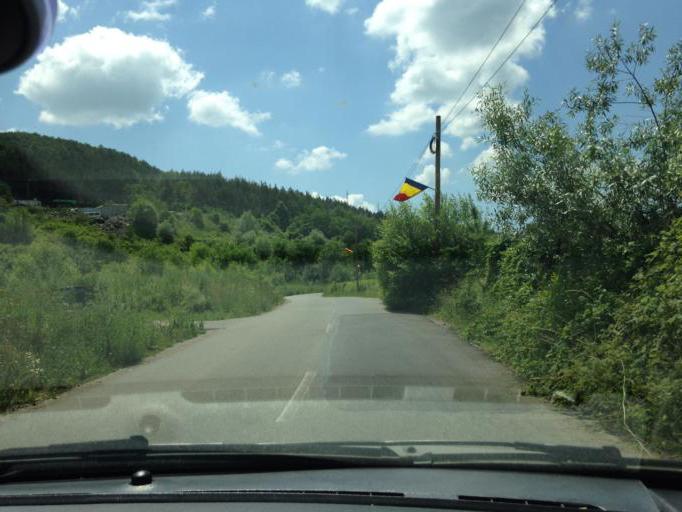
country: RO
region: Cluj
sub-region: Comuna Floresti
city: Floresti
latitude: 46.7500
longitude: 23.5361
